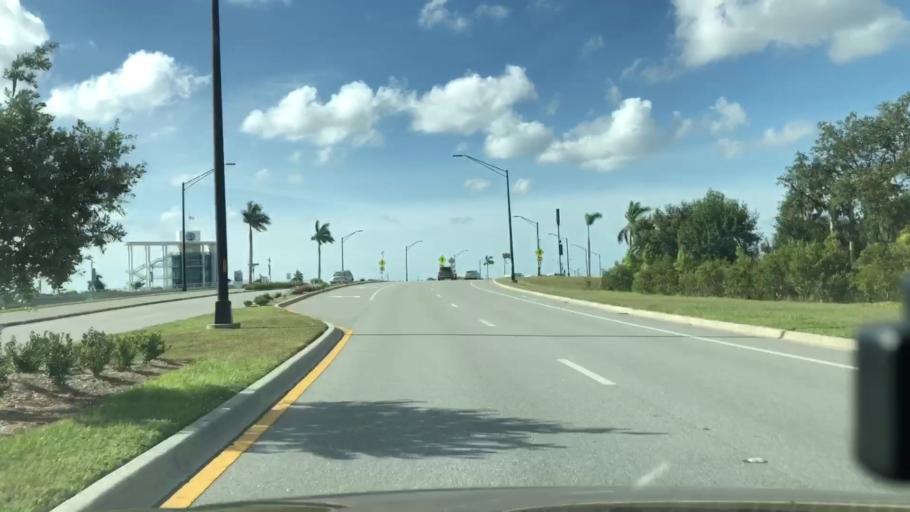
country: US
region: Florida
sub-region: Sarasota County
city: The Meadows
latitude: 27.3753
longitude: -82.4489
